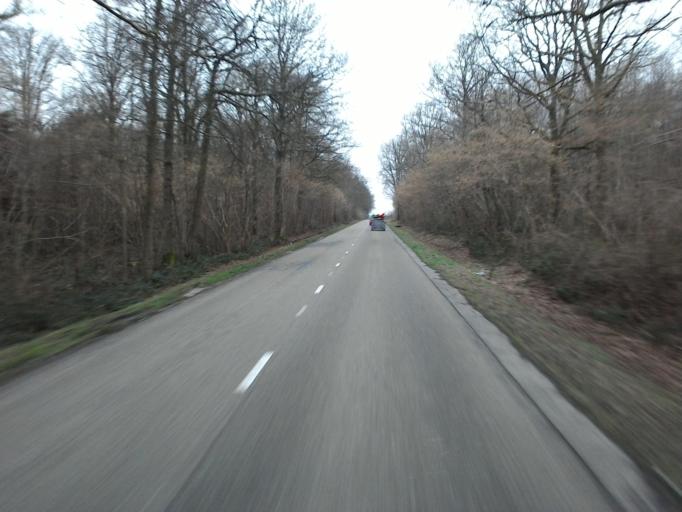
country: BE
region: Wallonia
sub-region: Province de Namur
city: Beauraing
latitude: 50.0466
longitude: 4.9694
